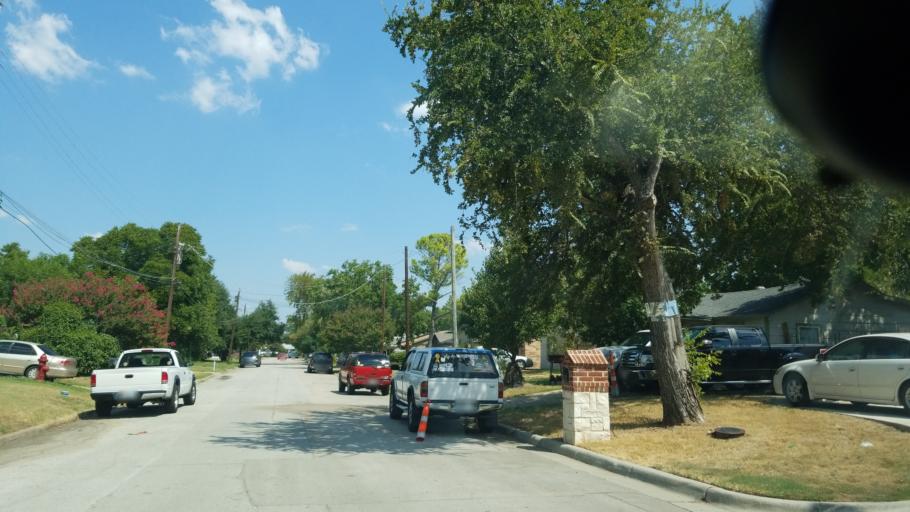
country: US
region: Texas
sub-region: Dallas County
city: Grand Prairie
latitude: 32.7131
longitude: -96.9891
